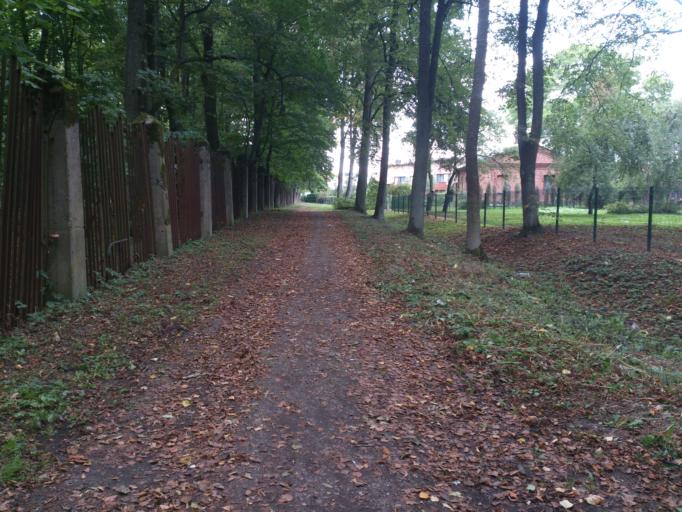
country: LT
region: Kauno apskritis
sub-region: Kaunas
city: Aleksotas
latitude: 54.8723
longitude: 23.9069
